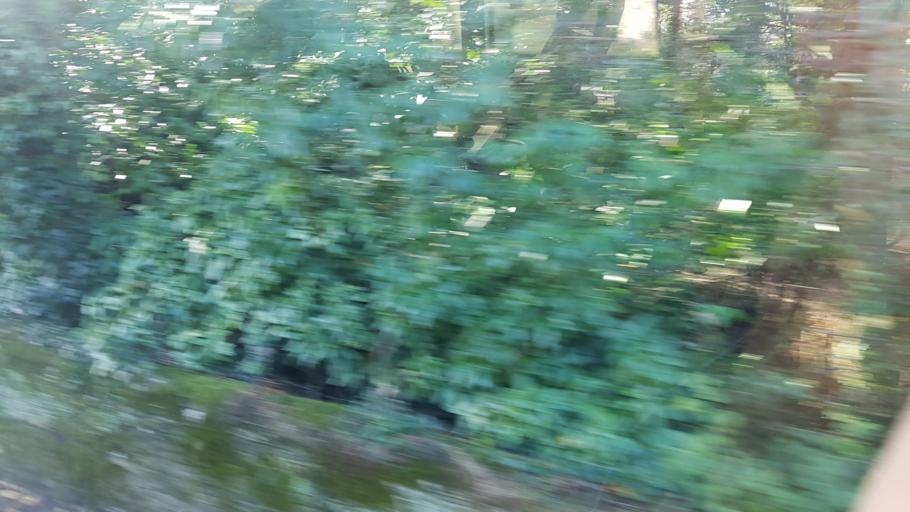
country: GB
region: England
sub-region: Isle of Wight
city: Chale
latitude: 50.6471
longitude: -1.3541
